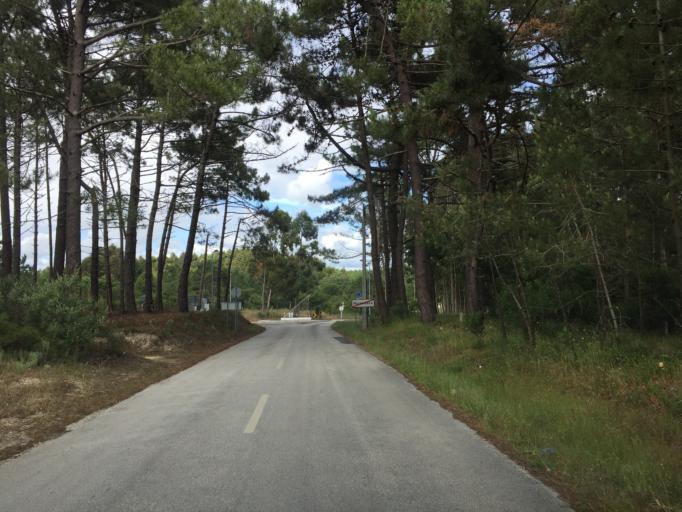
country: PT
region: Coimbra
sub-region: Figueira da Foz
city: Buarcos
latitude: 40.2146
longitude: -8.8849
